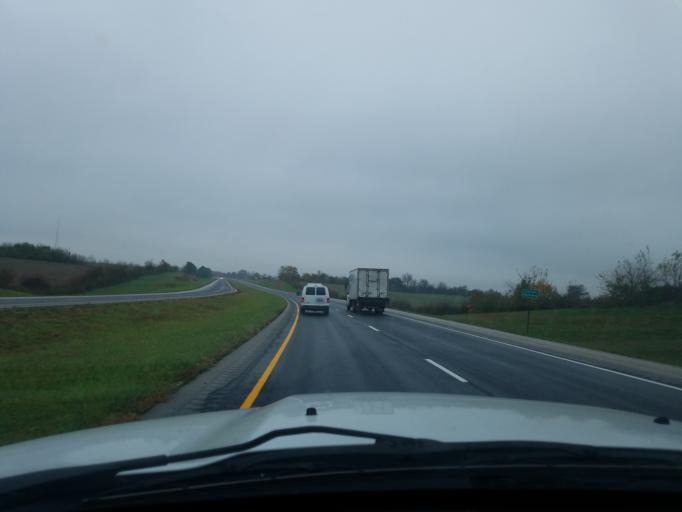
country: US
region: Kentucky
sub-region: Larue County
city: Hodgenville
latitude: 37.5601
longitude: -85.7467
